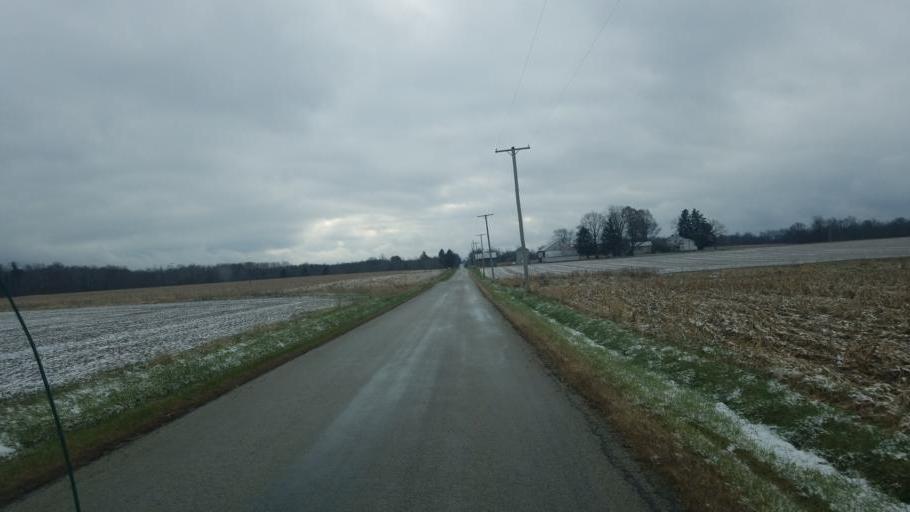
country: US
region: Ohio
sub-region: Richland County
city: Shelby
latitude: 40.8782
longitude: -82.5521
